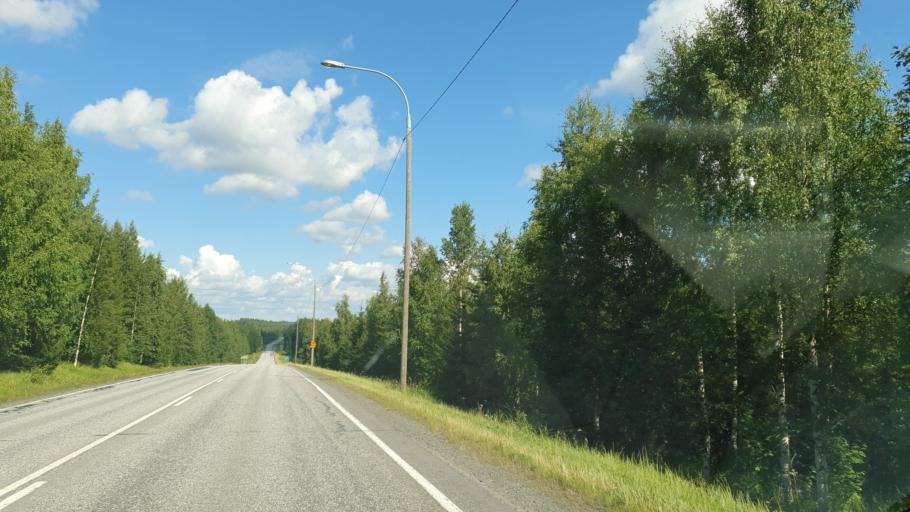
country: FI
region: Northern Savo
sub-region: Ylae-Savo
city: Sonkajaervi
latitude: 63.6988
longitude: 27.3564
